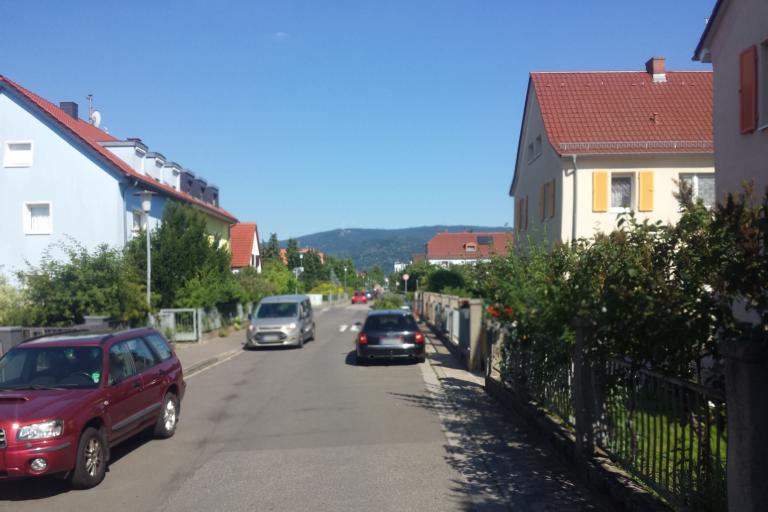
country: DE
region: Baden-Wuerttemberg
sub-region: Karlsruhe Region
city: Eppelheim
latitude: 49.4104
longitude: 8.6514
